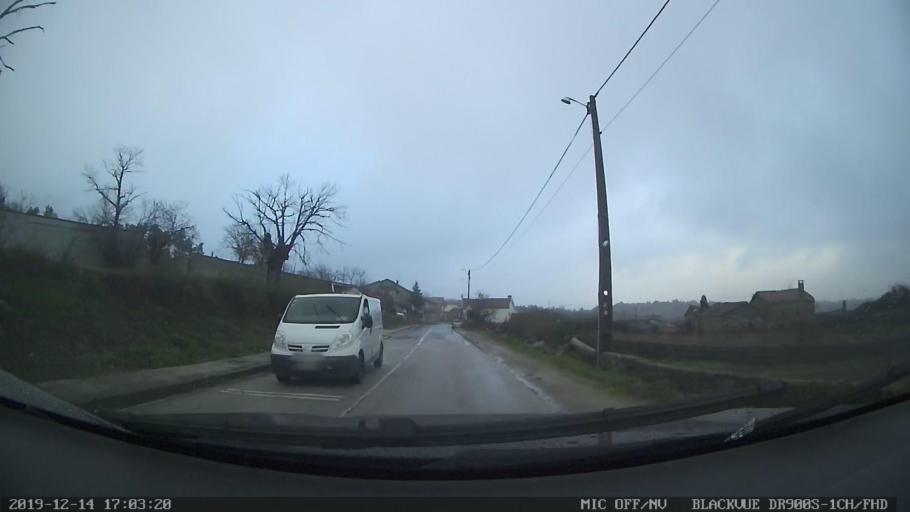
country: PT
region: Vila Real
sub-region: Vila Pouca de Aguiar
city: Vila Pouca de Aguiar
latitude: 41.4421
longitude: -7.5711
